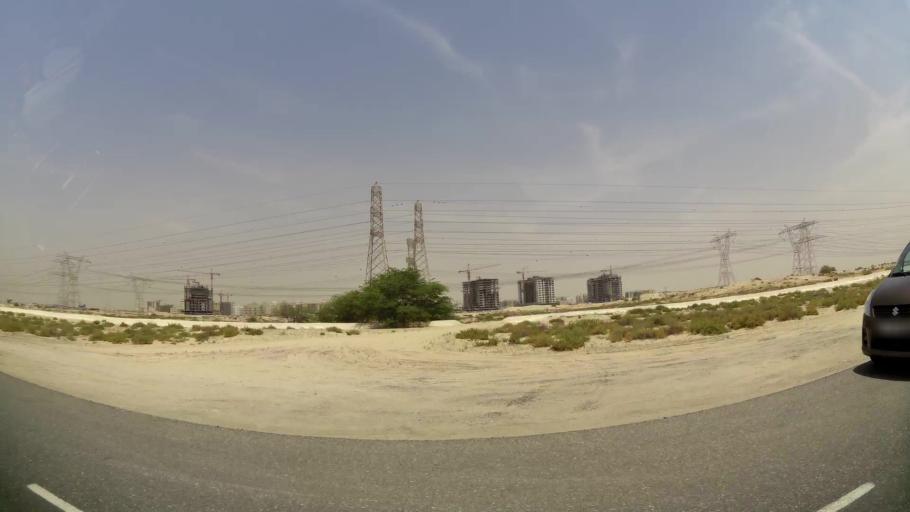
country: AE
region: Ash Shariqah
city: Sharjah
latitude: 25.1940
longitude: 55.3894
